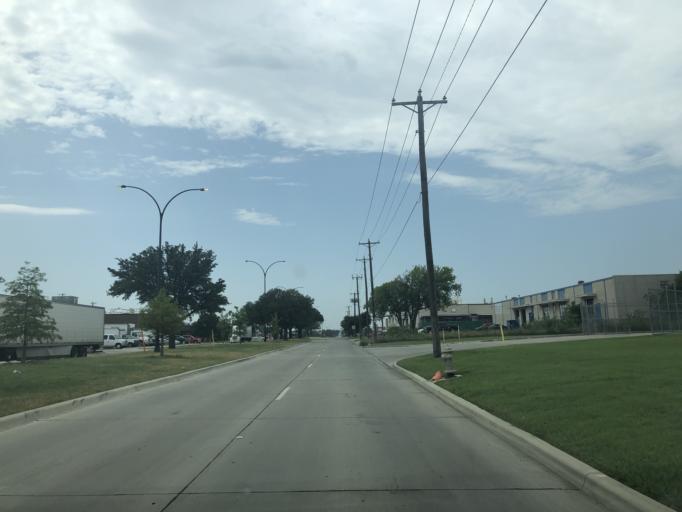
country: US
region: Texas
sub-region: Dallas County
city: Grand Prairie
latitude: 32.7553
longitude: -97.0459
